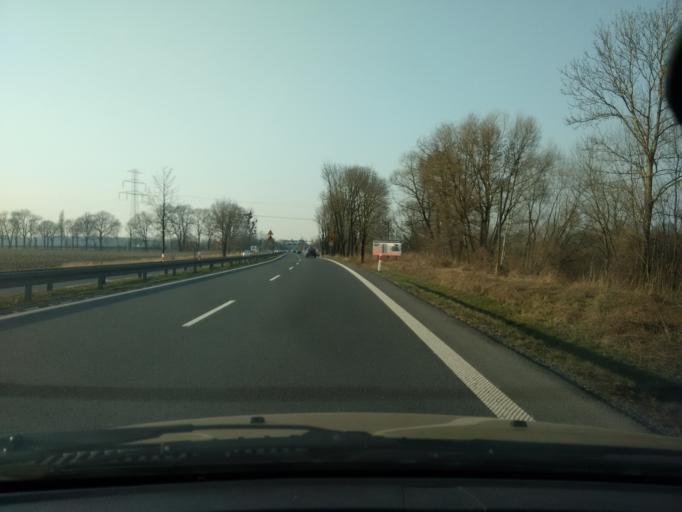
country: PL
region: Silesian Voivodeship
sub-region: Powiat cieszynski
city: Drogomysl
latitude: 49.8649
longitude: 18.7499
